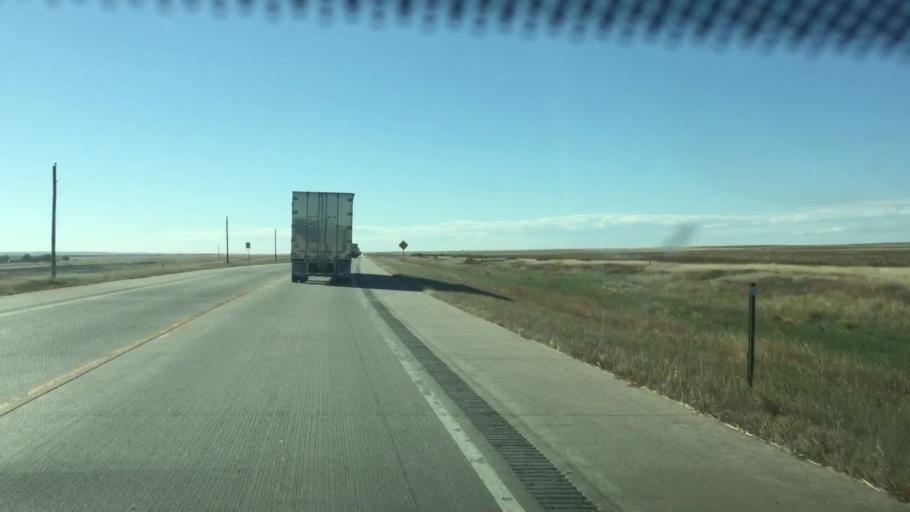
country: US
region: Colorado
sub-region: Kiowa County
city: Eads
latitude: 38.8270
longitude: -103.0199
